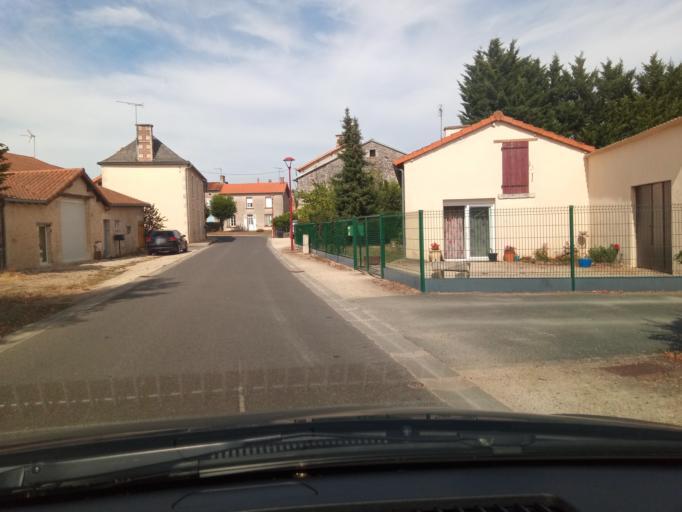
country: FR
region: Poitou-Charentes
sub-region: Departement de la Vienne
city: Chauvigny
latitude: 46.5545
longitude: 0.7454
